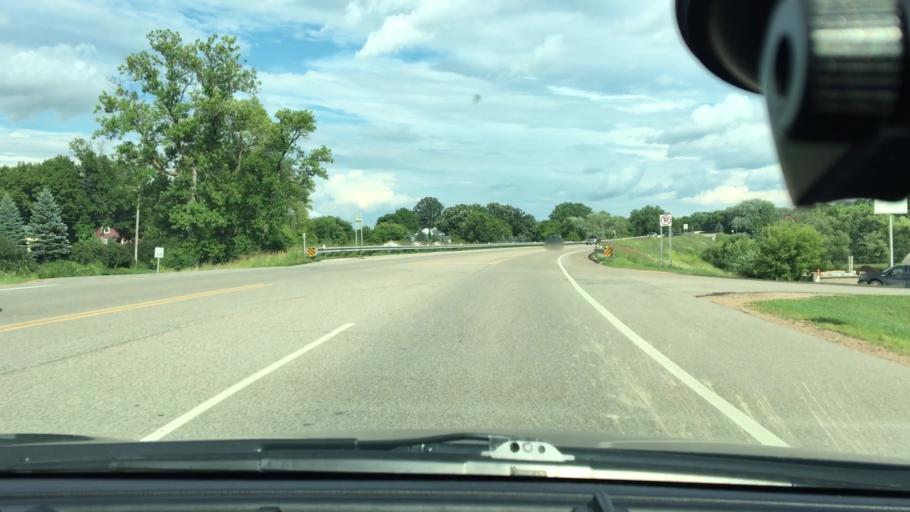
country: US
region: Minnesota
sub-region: Carver County
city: Victoria
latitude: 44.8602
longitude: -93.6713
